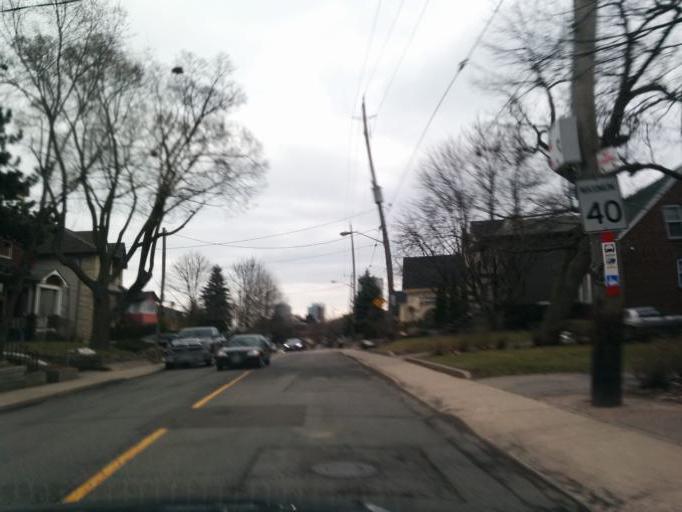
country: CA
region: Ontario
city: Toronto
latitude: 43.6425
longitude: -79.4760
